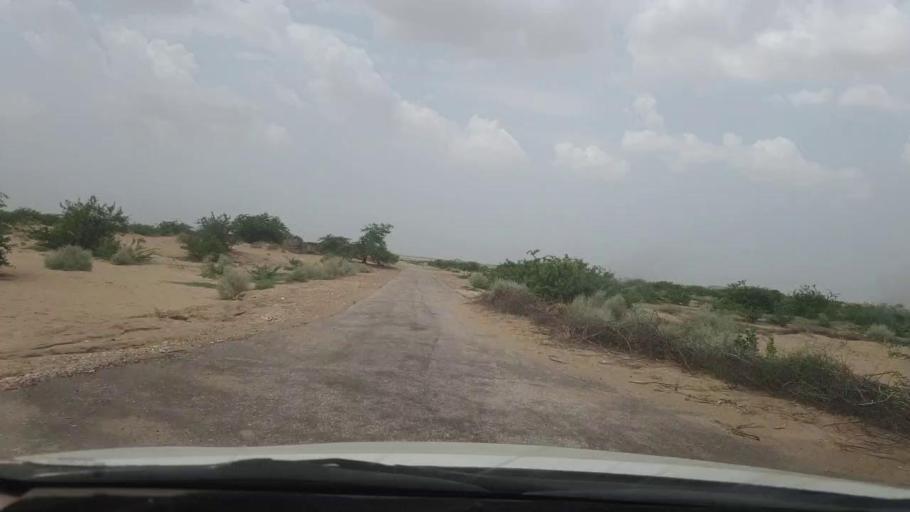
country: PK
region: Sindh
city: Khairpur
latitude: 27.3967
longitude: 68.9804
